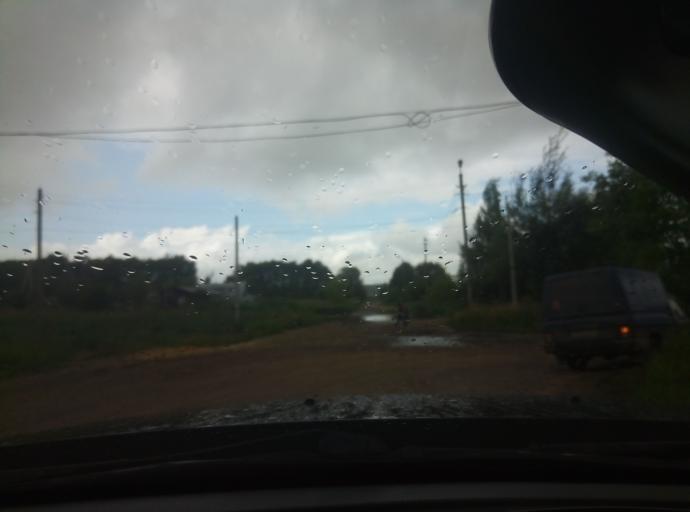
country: RU
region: Tula
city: Bolokhovo
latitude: 54.0791
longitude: 37.8187
